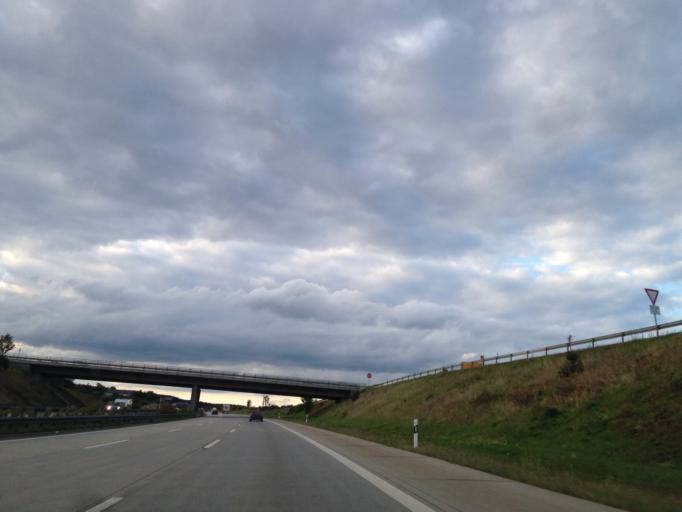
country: DE
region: Thuringia
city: Birkenhugel
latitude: 50.4427
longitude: 11.8033
